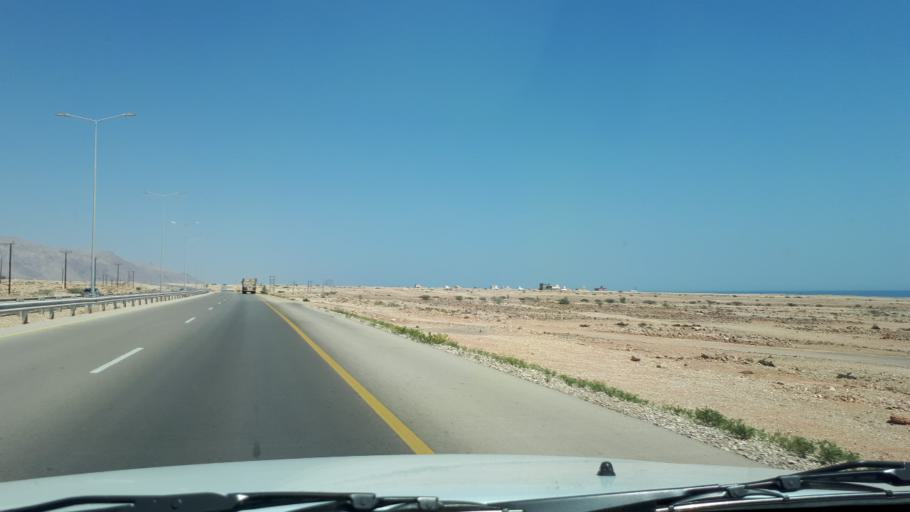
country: OM
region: Ash Sharqiyah
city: Sur
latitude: 22.7338
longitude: 59.3397
